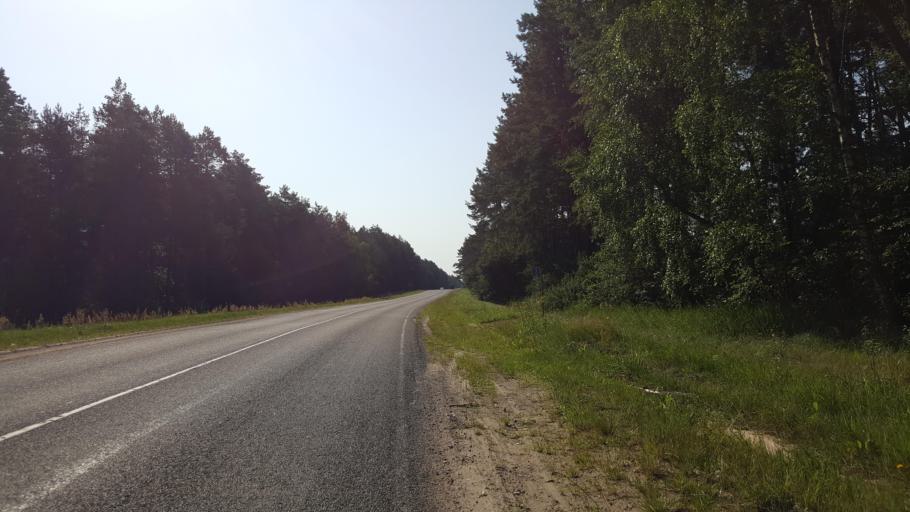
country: BY
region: Brest
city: Kamyanyets
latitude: 52.3845
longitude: 23.8579
